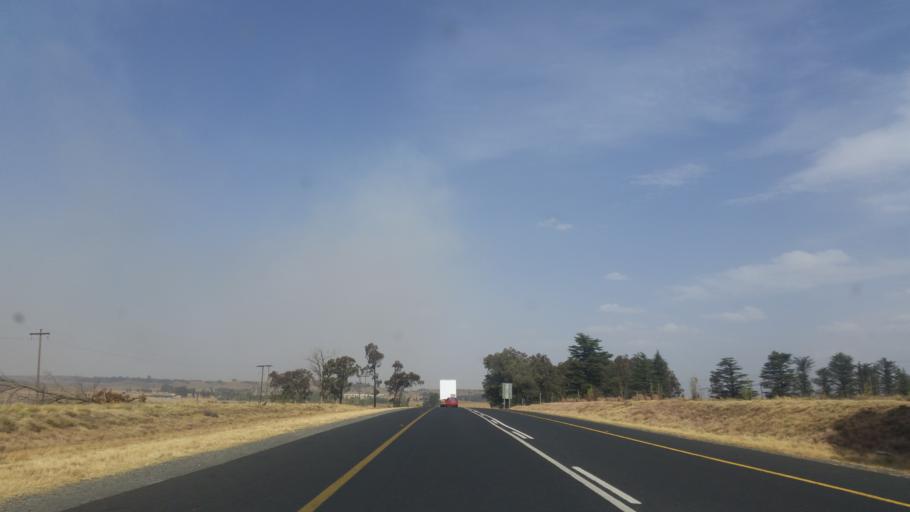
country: ZA
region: Orange Free State
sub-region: Thabo Mofutsanyana District Municipality
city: Bethlehem
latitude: -28.2685
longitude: 28.3654
